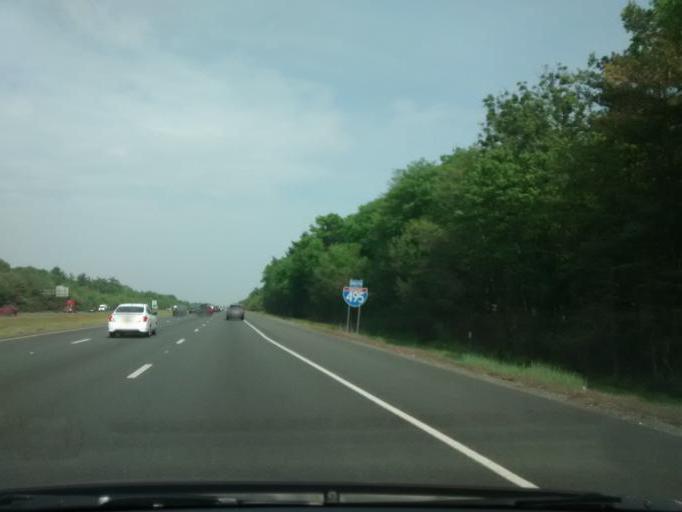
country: US
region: Massachusetts
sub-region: Bristol County
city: Raynham
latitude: 41.9616
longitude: -71.1138
